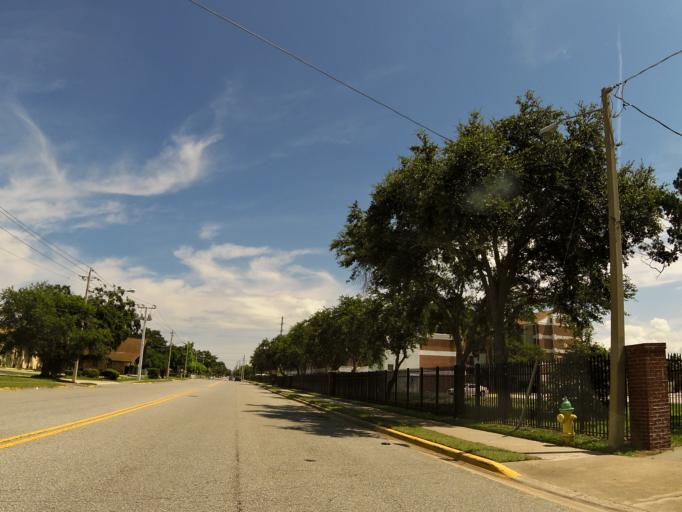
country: US
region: Florida
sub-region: Volusia County
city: Daytona Beach
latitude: 29.2118
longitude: -81.0303
